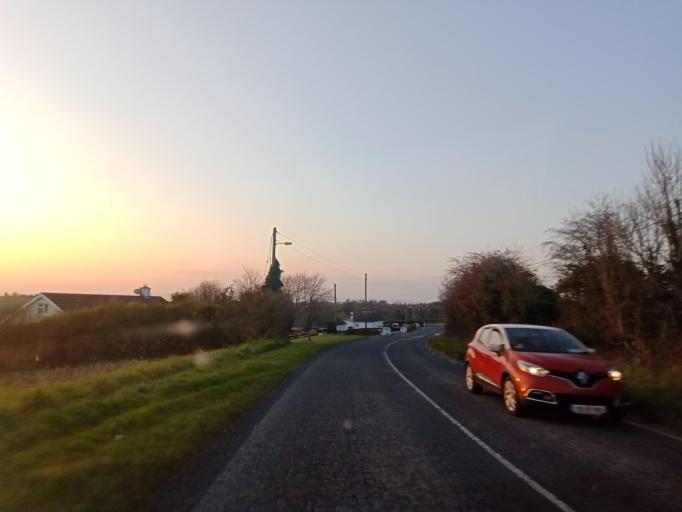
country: IE
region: Leinster
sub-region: Laois
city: Abbeyleix
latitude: 52.8972
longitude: -7.3173
